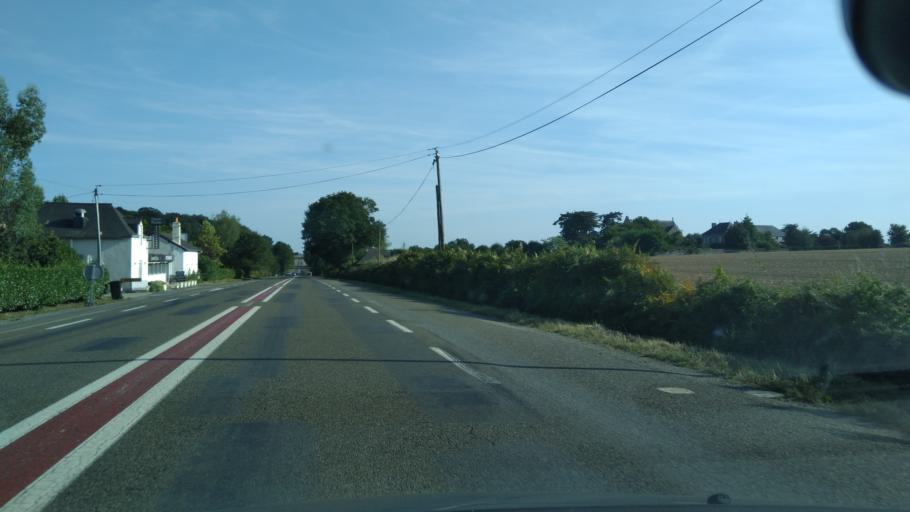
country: FR
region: Pays de la Loire
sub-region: Departement de la Mayenne
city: Entrammes
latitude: 48.0258
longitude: -0.7350
